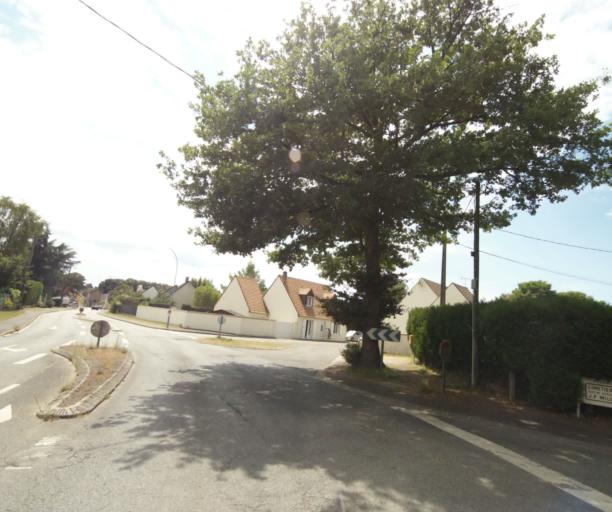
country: FR
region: Ile-de-France
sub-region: Departement de Seine-et-Marne
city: Chailly-en-Biere
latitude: 48.4704
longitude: 2.6095
